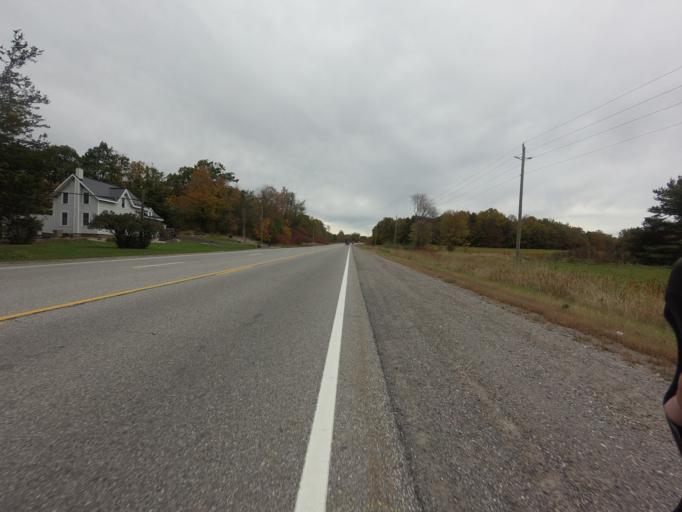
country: CA
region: Ontario
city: Gananoque
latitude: 44.4378
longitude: -76.2822
